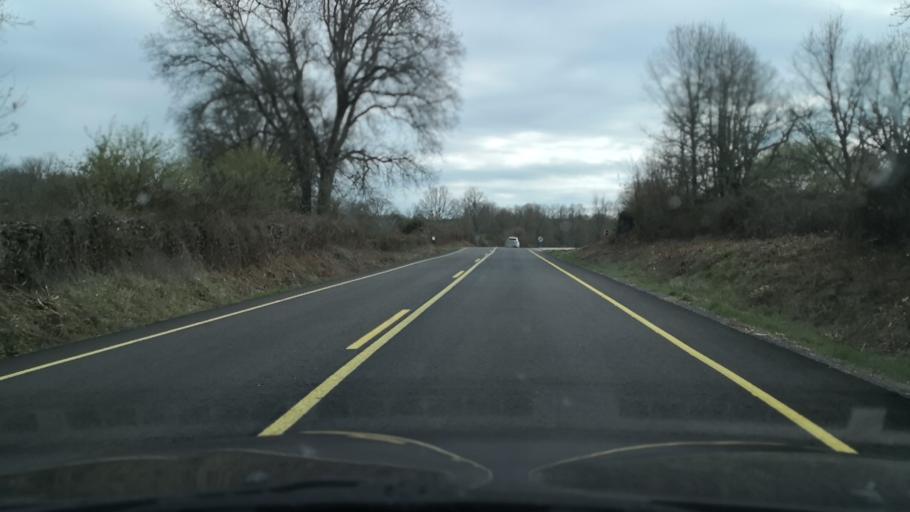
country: ES
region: Castille and Leon
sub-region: Provincia de Salamanca
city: Penaparda
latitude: 40.2758
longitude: -6.6795
